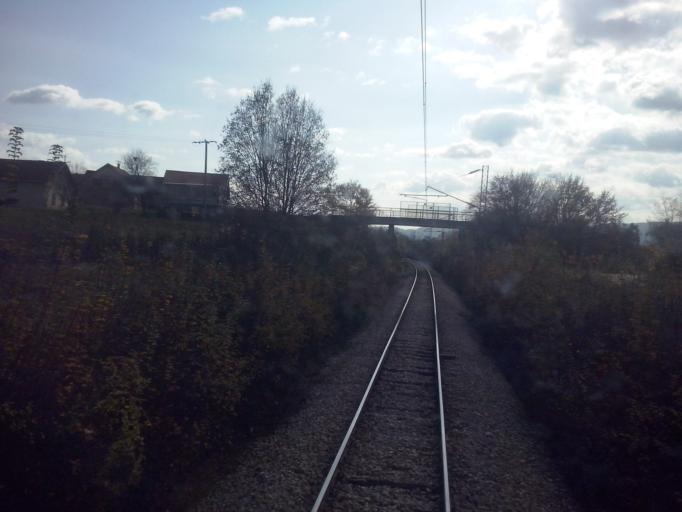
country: RS
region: Central Serbia
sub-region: Zlatiborski Okrug
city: Pozega
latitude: 43.8667
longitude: 20.0108
